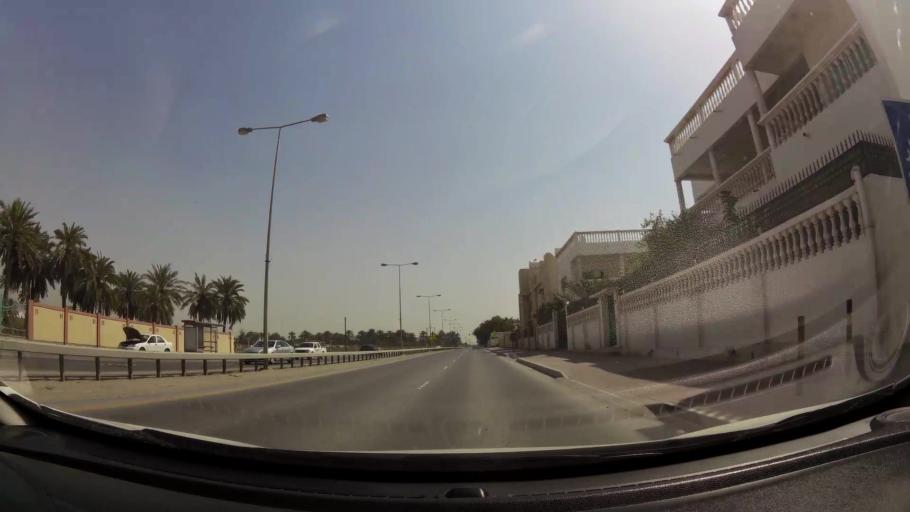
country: BH
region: Manama
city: Jidd Hafs
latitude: 26.2060
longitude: 50.4580
